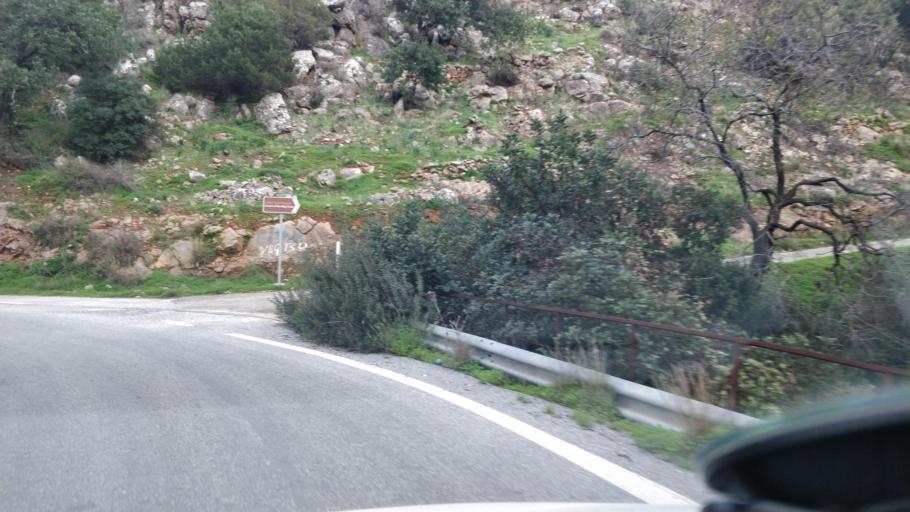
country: GR
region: Crete
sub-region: Nomos Lasithiou
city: Agios Nikolaos
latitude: 35.1108
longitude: 25.7214
